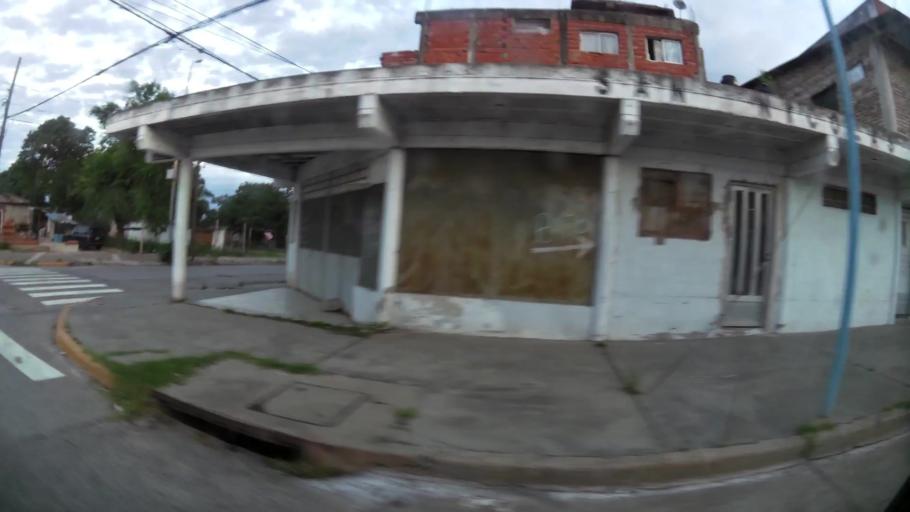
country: AR
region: Buenos Aires
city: San Nicolas de los Arroyos
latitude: -33.3237
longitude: -60.2239
